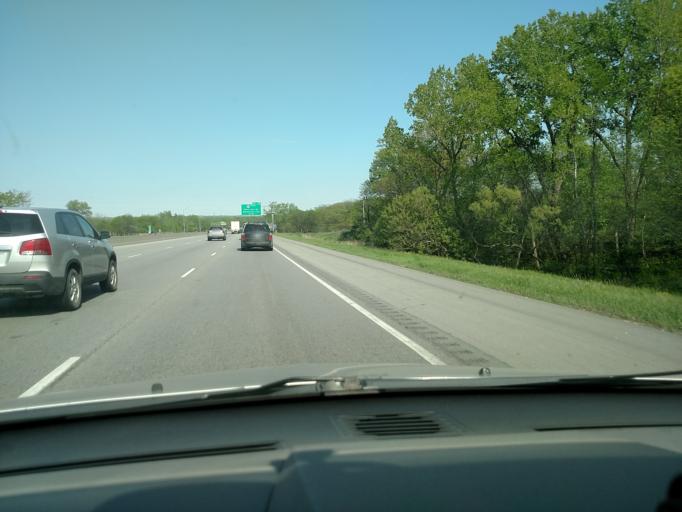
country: US
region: Iowa
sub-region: Polk County
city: Urbandale
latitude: 41.6525
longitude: -93.7197
